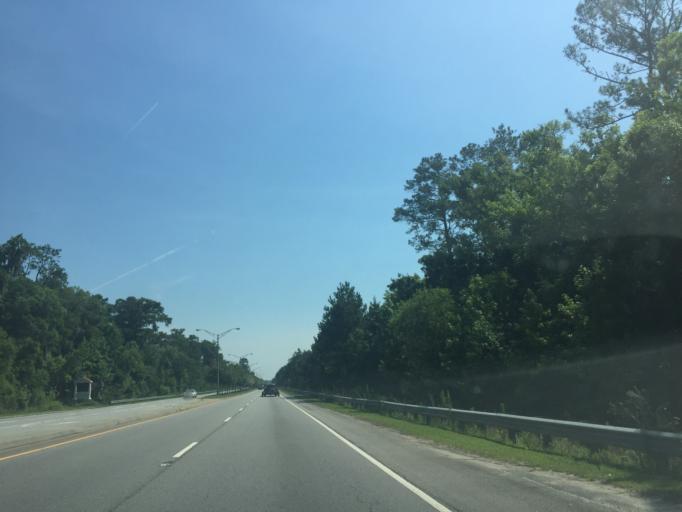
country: US
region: Georgia
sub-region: Bryan County
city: Richmond Hill
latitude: 31.9570
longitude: -81.3066
